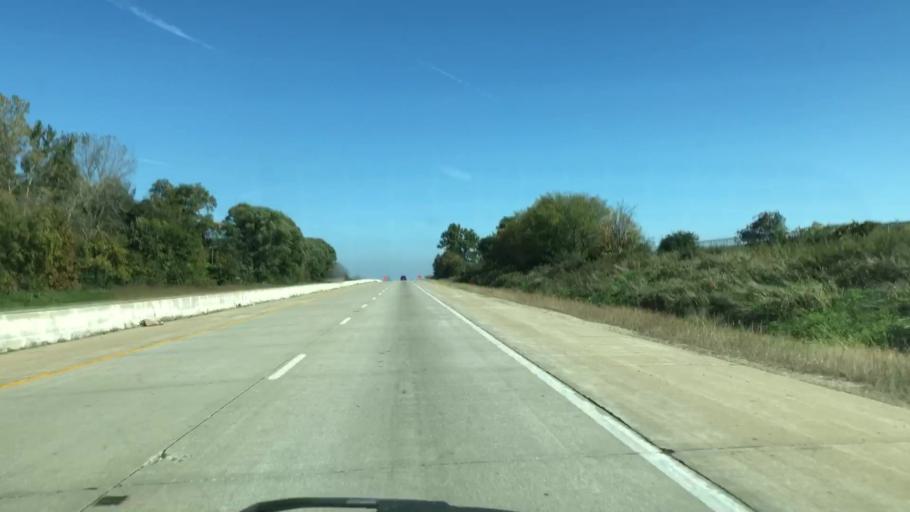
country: US
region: Indiana
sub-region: Elkhart County
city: Elkhart
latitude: 41.6368
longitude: -85.9797
